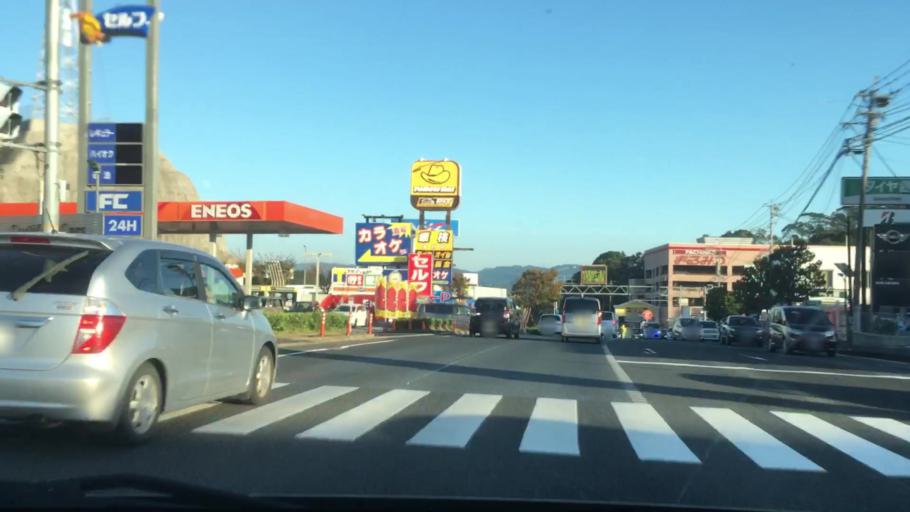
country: JP
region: Nagasaki
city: Sasebo
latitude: 33.1577
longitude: 129.7661
